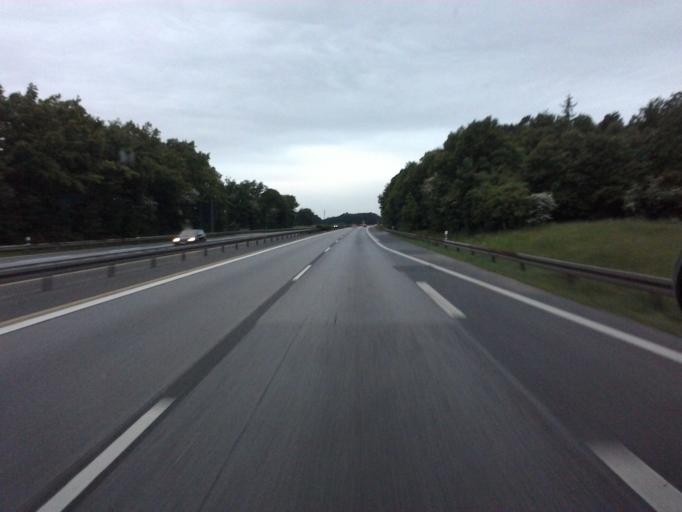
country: DE
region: Bavaria
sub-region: Regierungsbezirk Mittelfranken
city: Wachenroth
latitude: 49.7312
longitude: 10.7215
